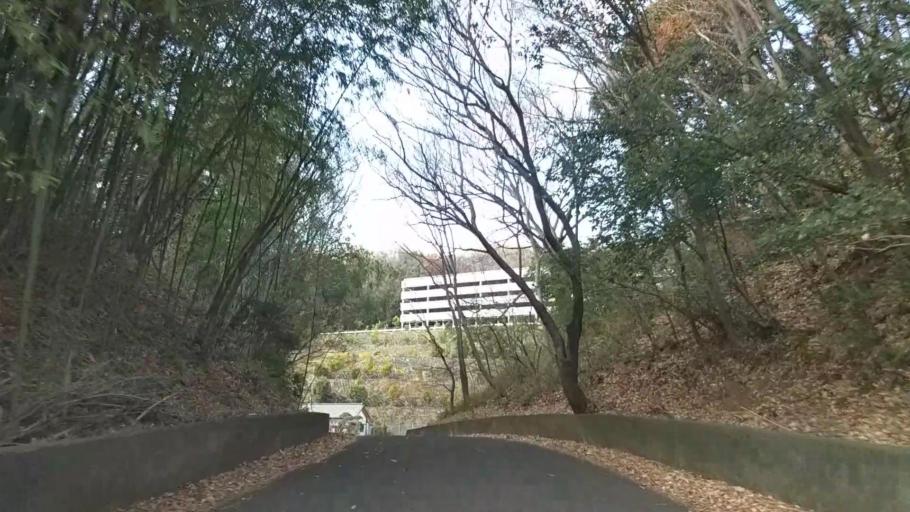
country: JP
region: Kanagawa
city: Isehara
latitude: 35.4190
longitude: 139.3172
